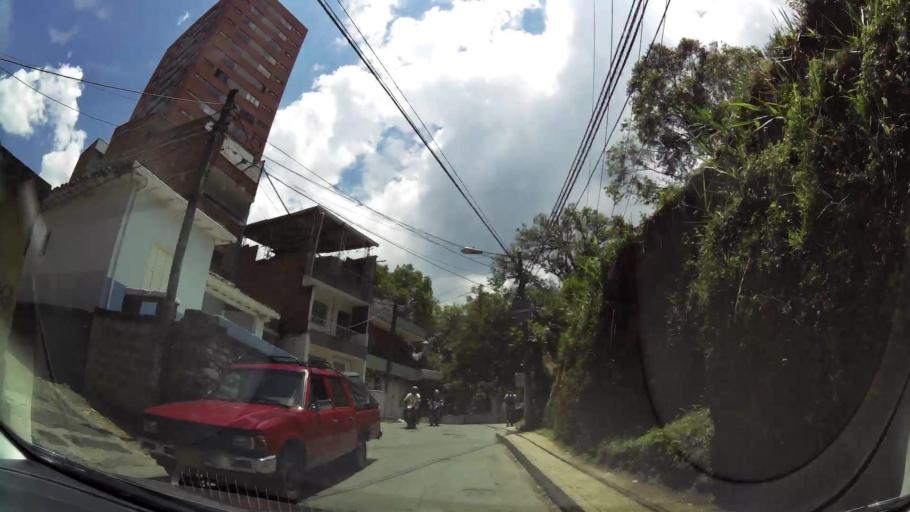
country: CO
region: Antioquia
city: La Estrella
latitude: 6.1634
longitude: -75.6362
